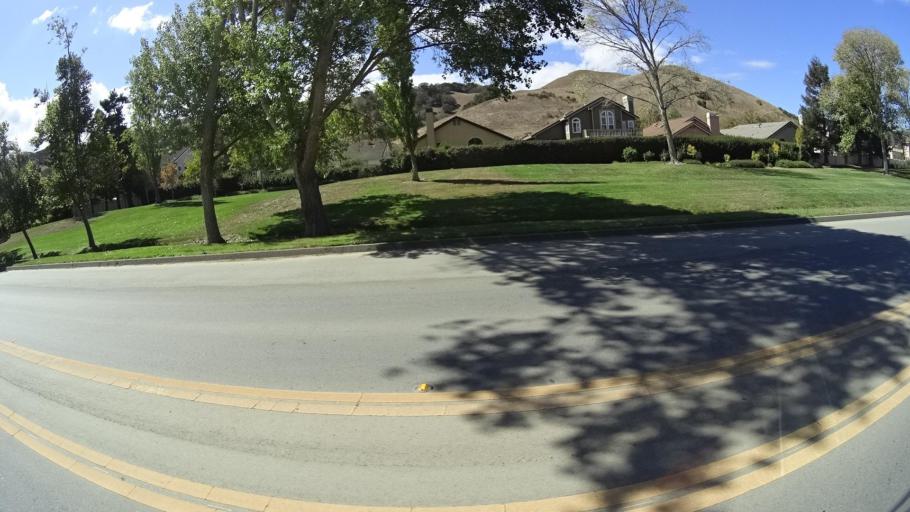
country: US
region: California
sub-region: Monterey County
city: Salinas
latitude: 36.6193
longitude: -121.6614
